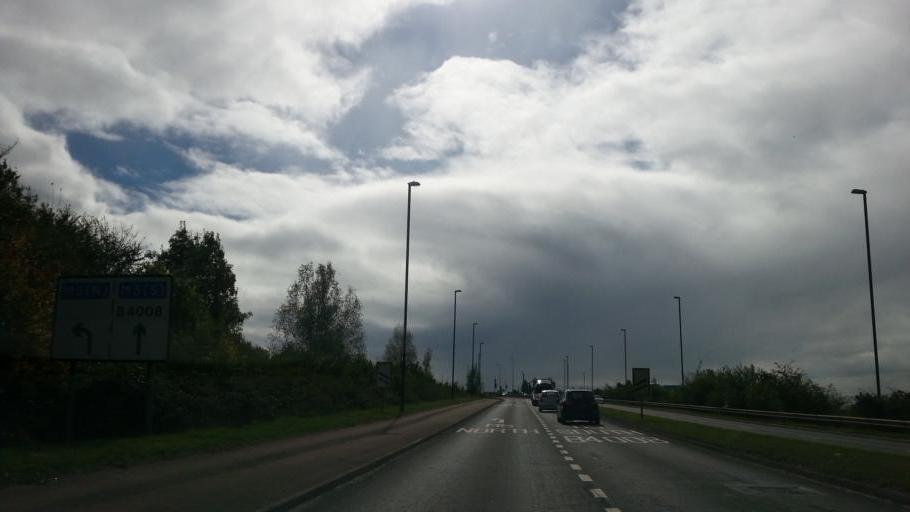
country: GB
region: England
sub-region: Gloucestershire
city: Stonehouse
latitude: 51.8011
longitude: -2.2894
